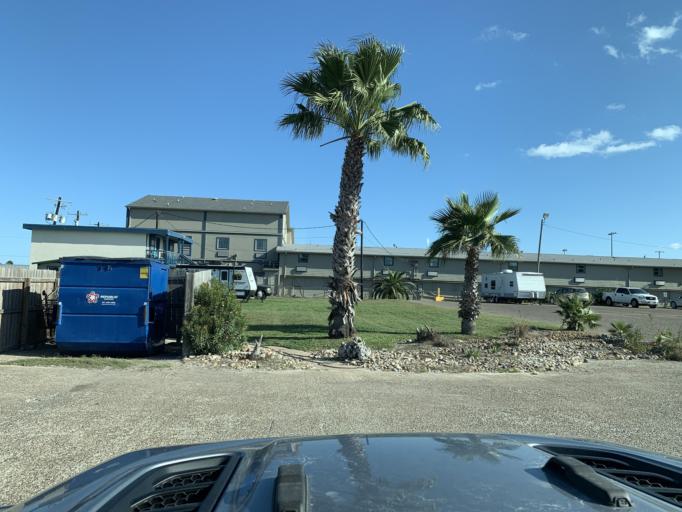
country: US
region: Texas
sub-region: Nueces County
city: Port Aransas
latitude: 27.8308
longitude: -97.0657
